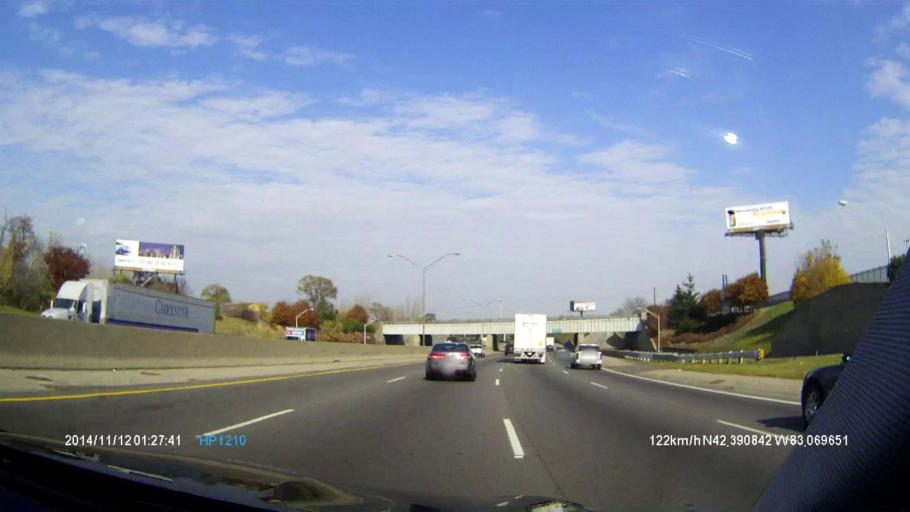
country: US
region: Michigan
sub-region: Wayne County
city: Hamtramck
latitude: 42.3911
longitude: -83.0696
